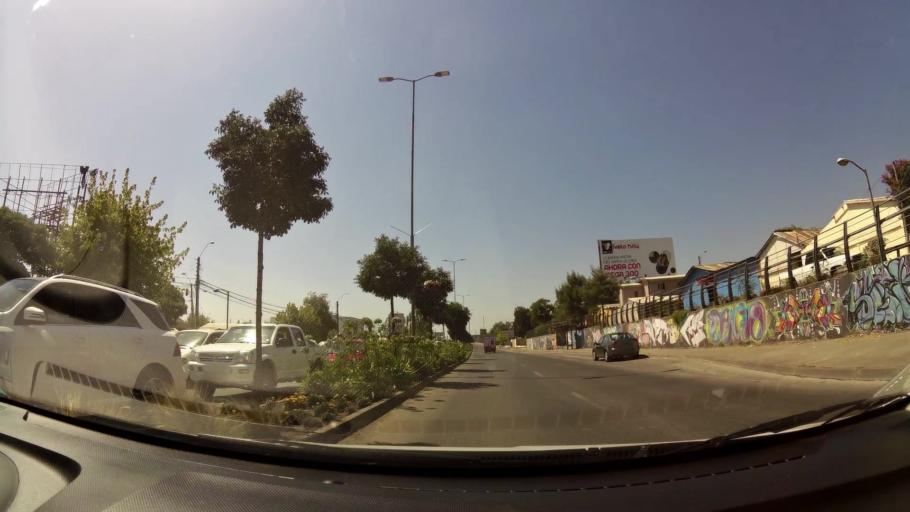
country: CL
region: Maule
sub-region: Provincia de Talca
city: Talca
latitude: -35.4280
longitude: -71.6393
